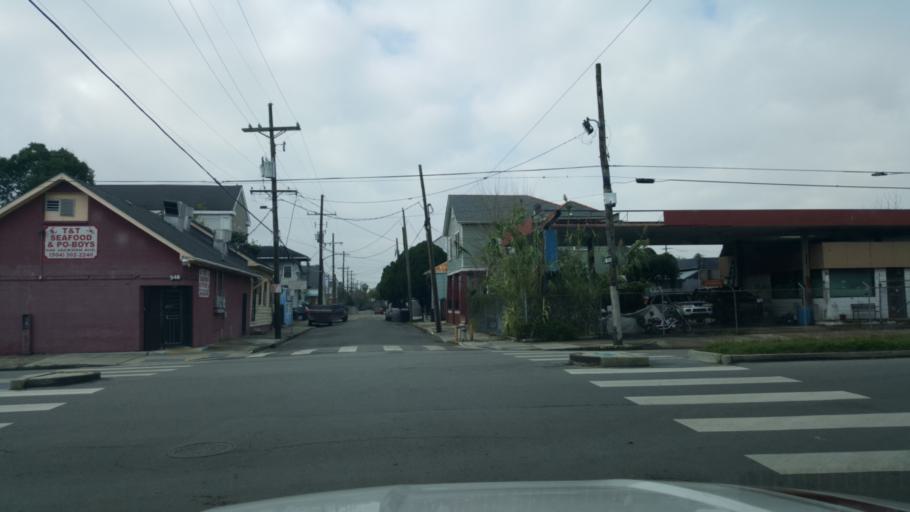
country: US
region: Louisiana
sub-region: Jefferson Parish
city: Gretna
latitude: 29.9257
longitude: -90.0732
